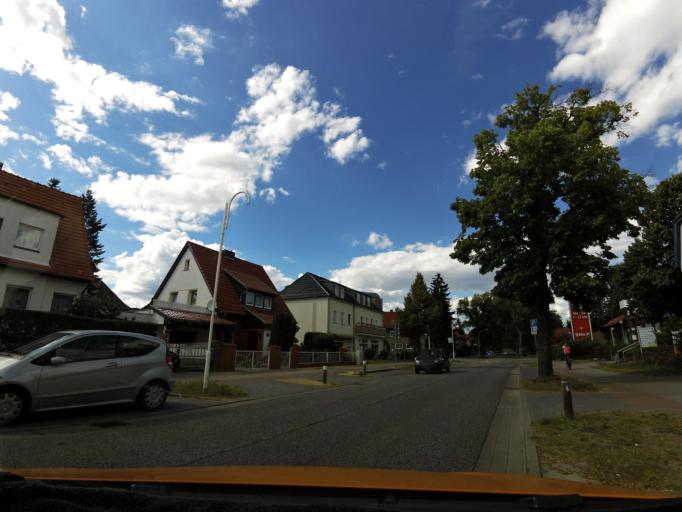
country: DE
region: Berlin
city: Lichtenrade
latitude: 52.3613
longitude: 13.4112
